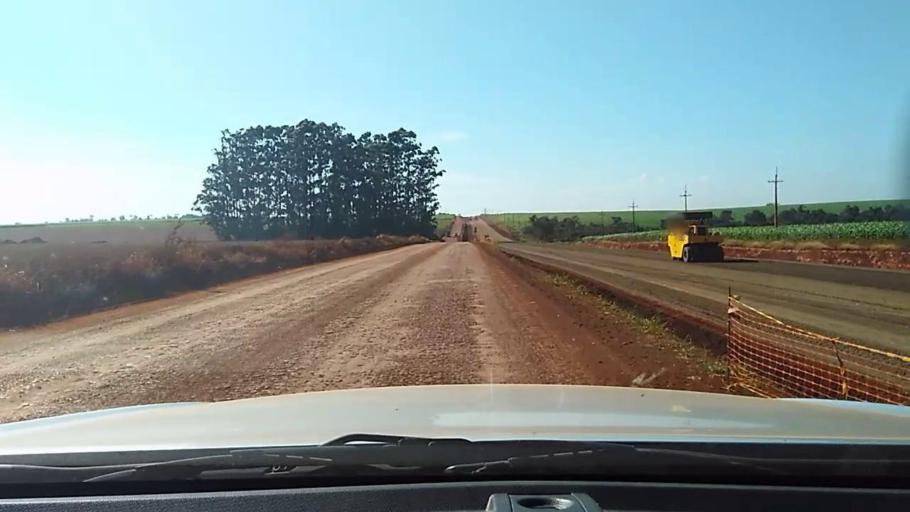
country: PY
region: Alto Parana
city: Naranjal
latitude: -25.9189
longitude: -55.4248
